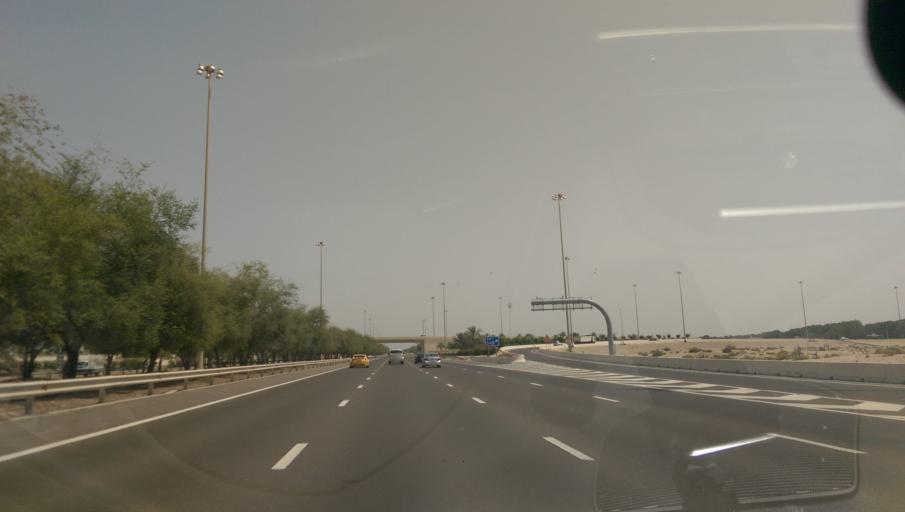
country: AE
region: Abu Dhabi
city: Abu Dhabi
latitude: 24.4614
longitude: 54.6778
